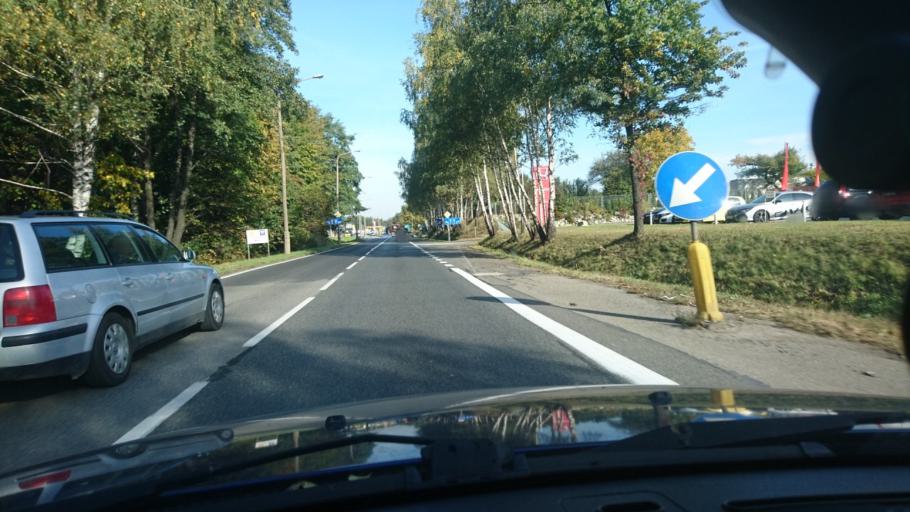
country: PL
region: Silesian Voivodeship
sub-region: Bielsko-Biala
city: Bielsko-Biala
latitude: 49.8529
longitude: 19.0285
